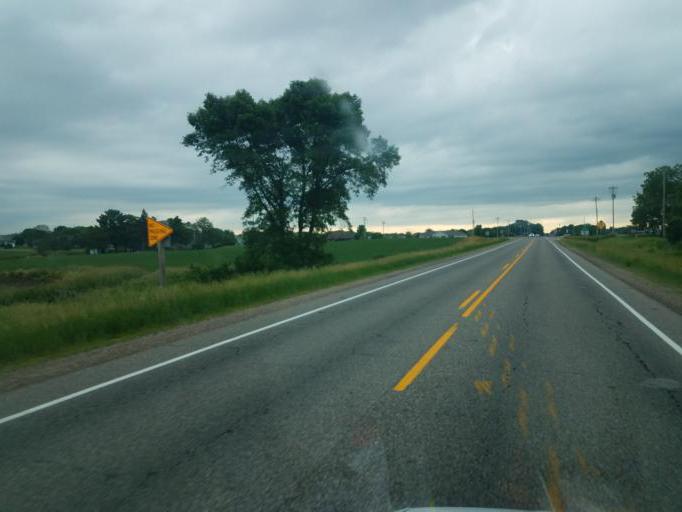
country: US
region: Wisconsin
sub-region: Juneau County
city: Mauston
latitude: 43.7891
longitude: -90.0945
